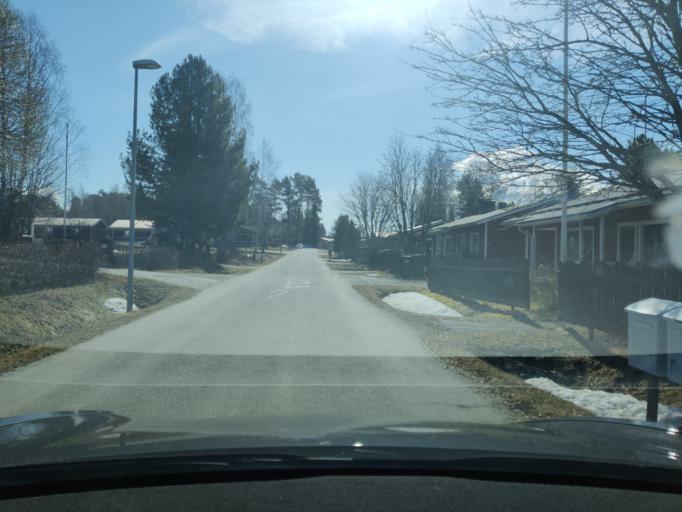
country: FI
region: Northern Savo
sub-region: Kuopio
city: Vehmersalmi
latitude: 62.7645
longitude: 28.0183
